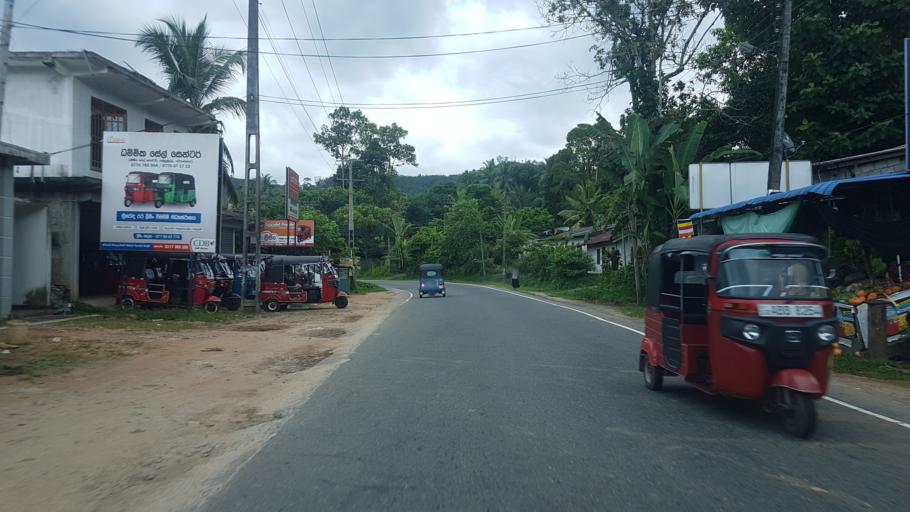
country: LK
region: Western
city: Hanwella Ihala
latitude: 7.0228
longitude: 80.2636
